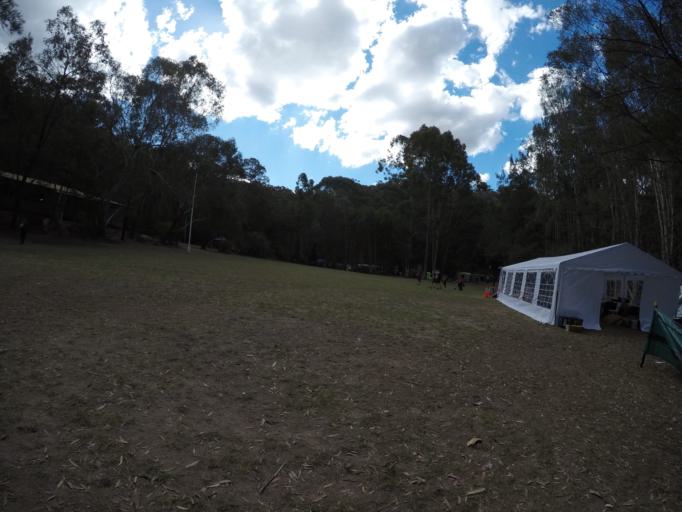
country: AU
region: New South Wales
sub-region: Hawkesbury
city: Pitt Town
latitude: -33.4702
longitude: 150.8908
